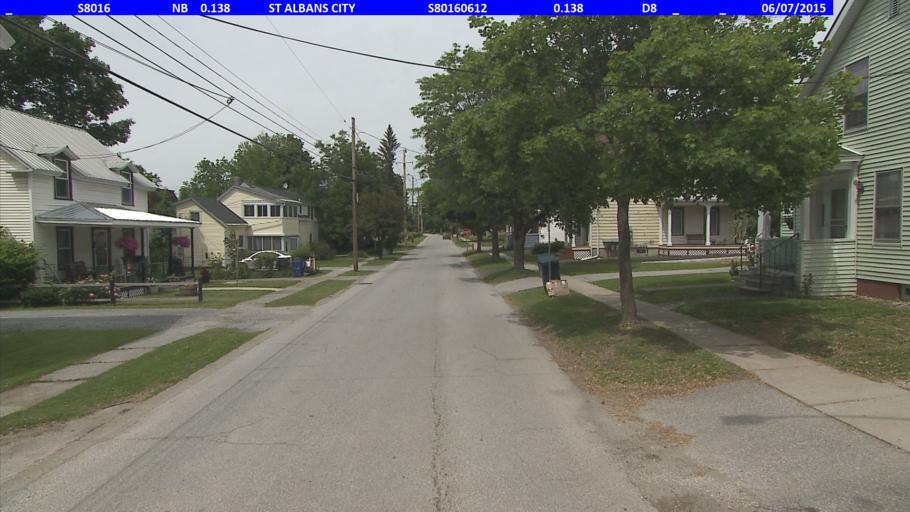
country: US
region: Vermont
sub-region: Franklin County
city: Saint Albans
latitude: 44.8078
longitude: -73.0811
